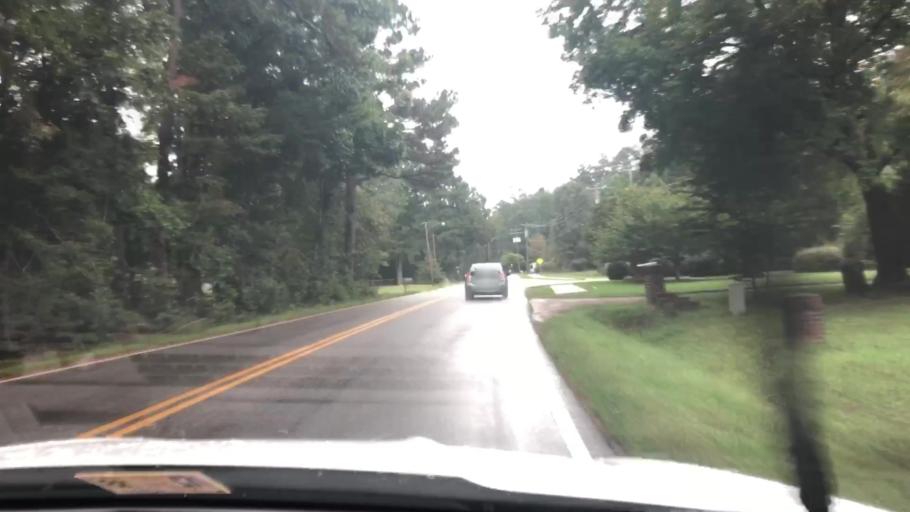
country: US
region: Virginia
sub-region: James City County
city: Williamsburg
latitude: 37.3167
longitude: -76.7833
